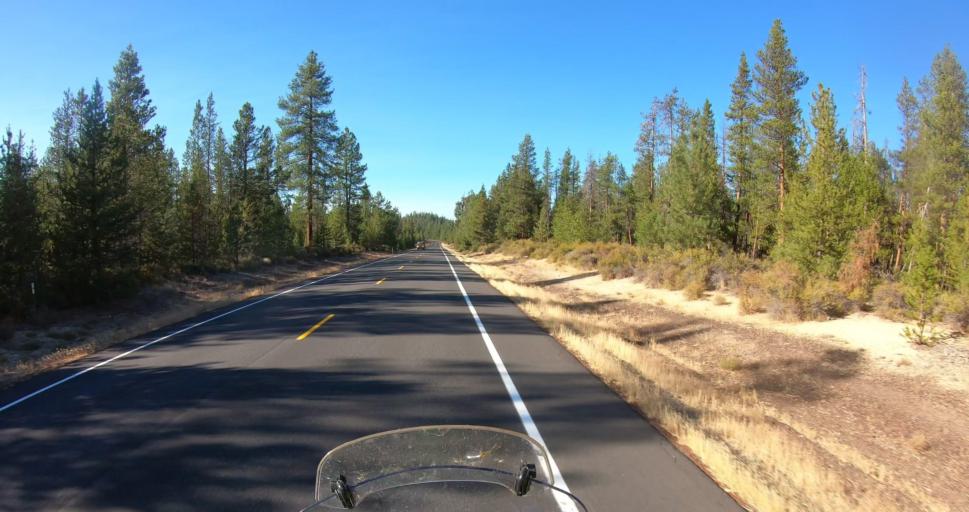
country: US
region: Oregon
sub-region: Deschutes County
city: La Pine
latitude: 43.4621
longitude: -121.3833
